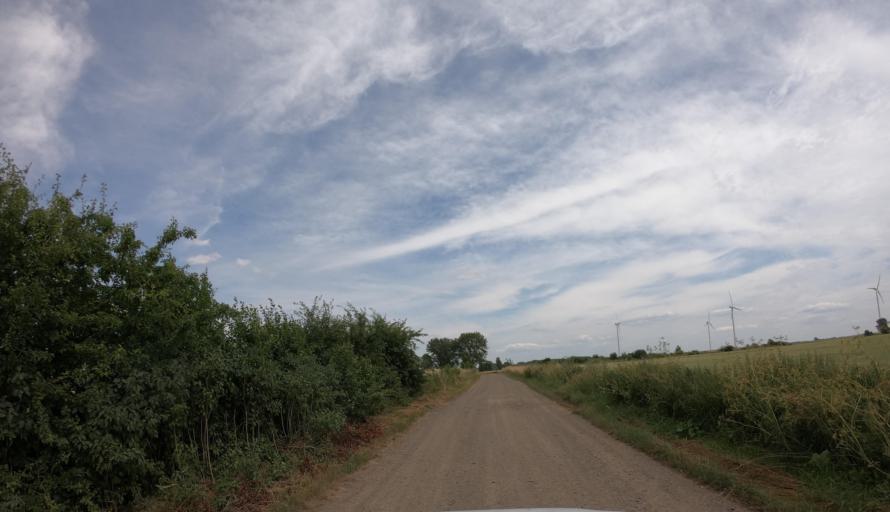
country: PL
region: West Pomeranian Voivodeship
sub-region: Powiat pyrzycki
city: Kozielice
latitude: 53.1101
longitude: 14.8210
